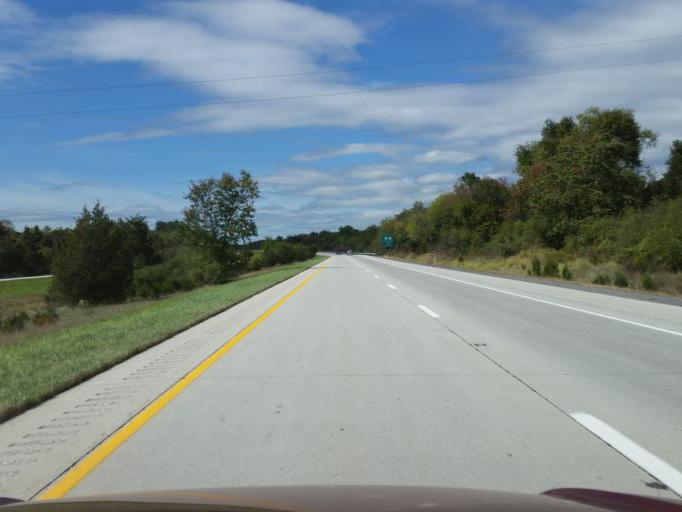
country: US
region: Pennsylvania
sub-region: Lancaster County
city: Elizabethtown
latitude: 40.1935
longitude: -76.6344
